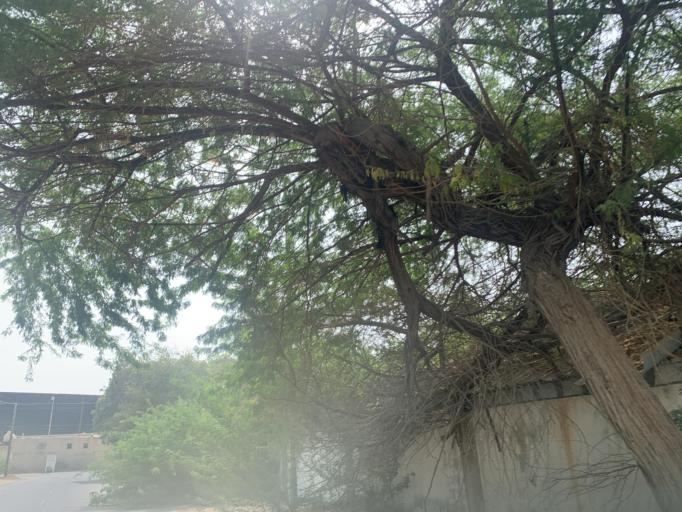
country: BH
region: Manama
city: Jidd Hafs
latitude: 26.2031
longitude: 50.4626
